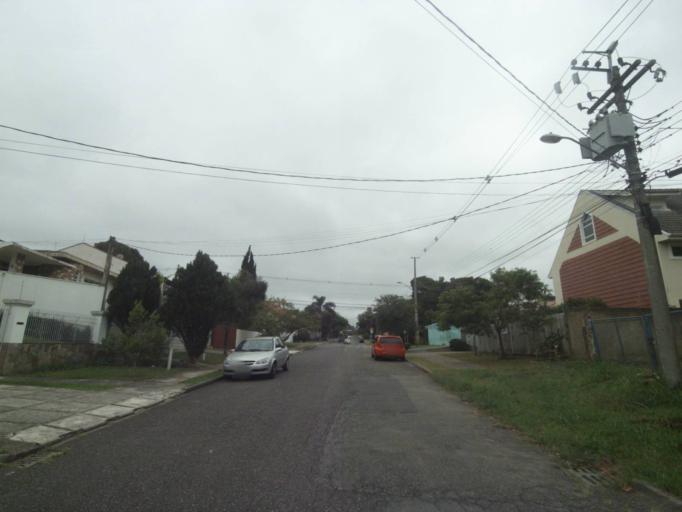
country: BR
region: Parana
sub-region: Curitiba
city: Curitiba
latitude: -25.4038
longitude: -49.2771
